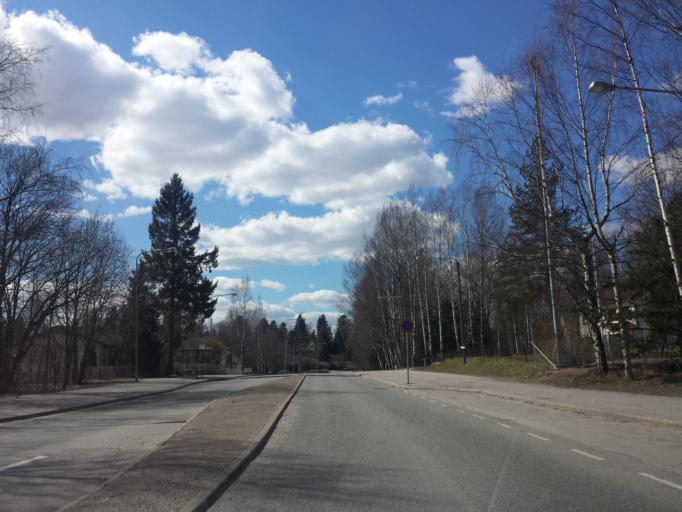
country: FI
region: Uusimaa
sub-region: Helsinki
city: Vantaa
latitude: 60.2703
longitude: 25.0597
